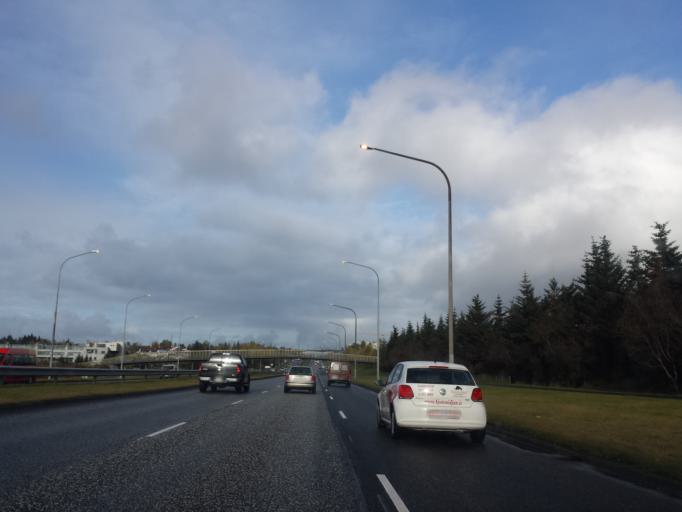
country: IS
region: Capital Region
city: Kopavogur
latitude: 64.1180
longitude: -21.8980
